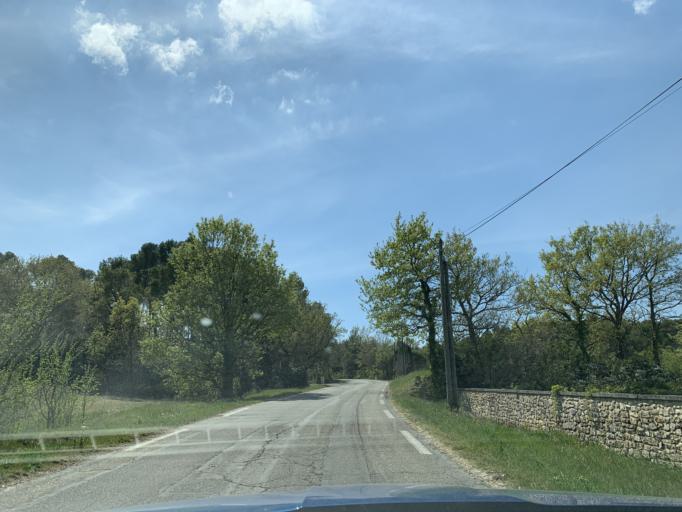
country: FR
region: Provence-Alpes-Cote d'Azur
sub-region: Departement du Vaucluse
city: Saint-Didier
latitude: 44.0024
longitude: 5.1075
